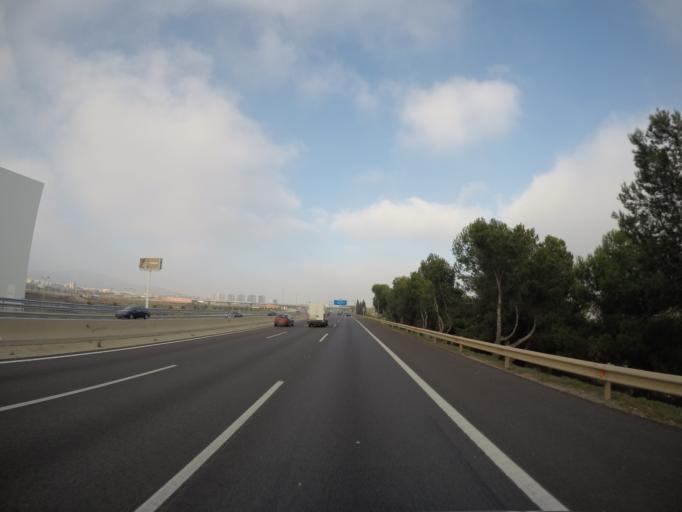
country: ES
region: Catalonia
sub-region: Provincia de Barcelona
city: Viladecans
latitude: 41.3001
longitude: 2.0216
